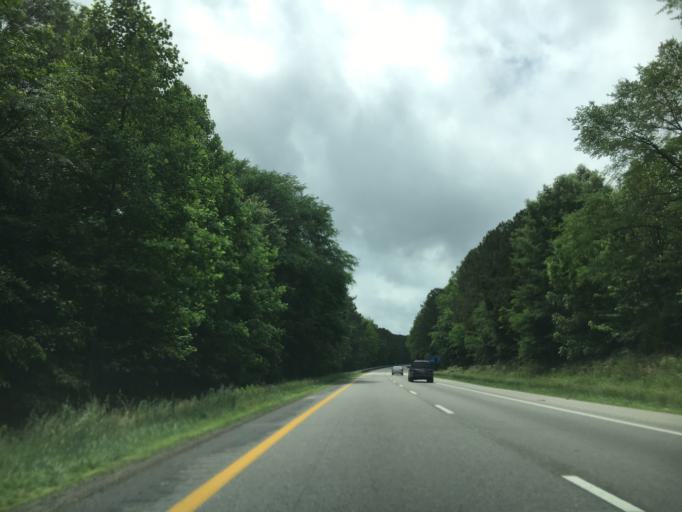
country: US
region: Virginia
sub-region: Brunswick County
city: Lawrenceville
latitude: 36.8521
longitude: -77.8635
